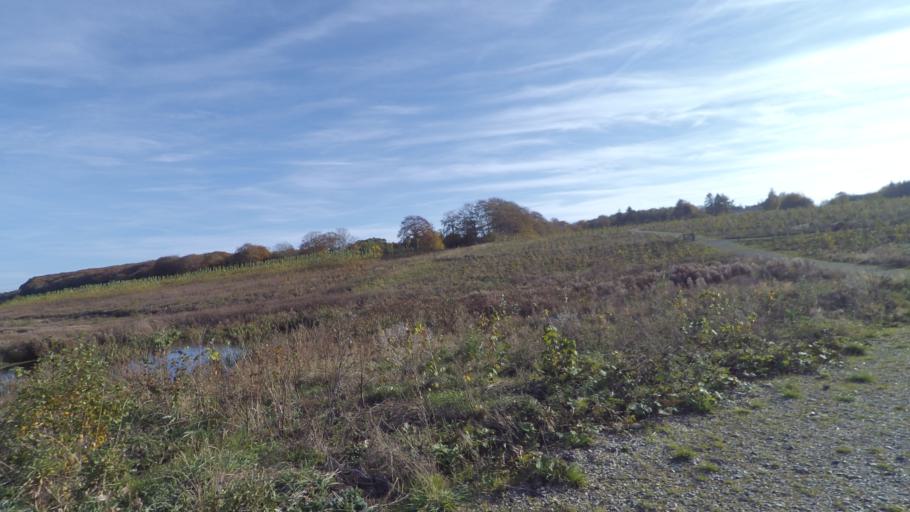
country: DK
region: Central Jutland
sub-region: Arhus Kommune
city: Framlev
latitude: 56.1260
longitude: 10.0222
